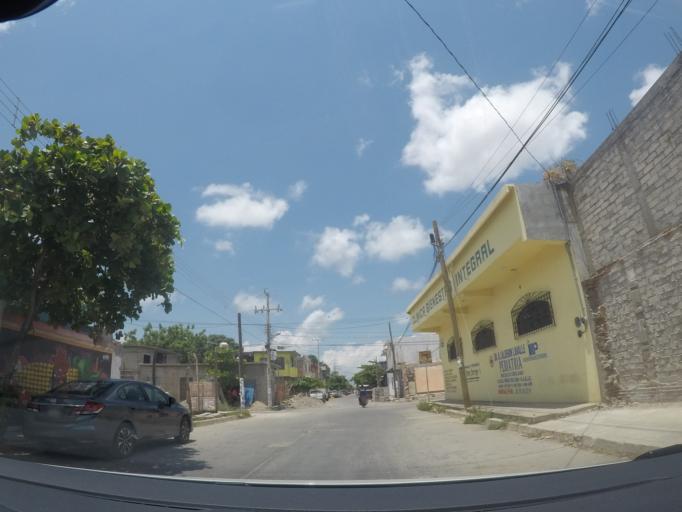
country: MX
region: Oaxaca
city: Juchitan de Zaragoza
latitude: 16.4409
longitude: -95.0166
